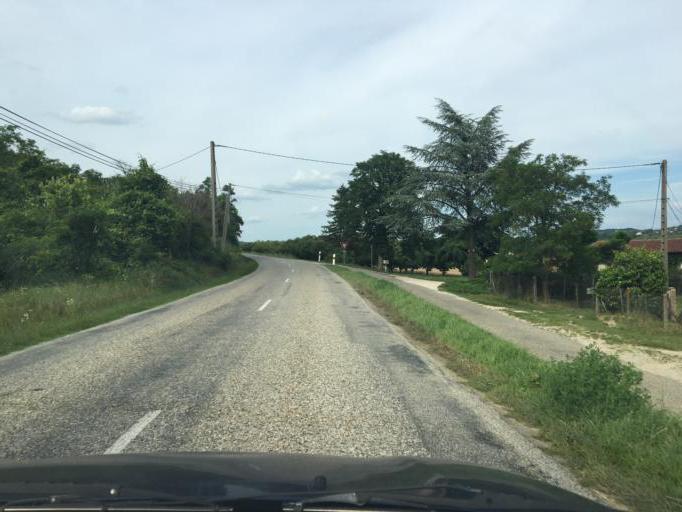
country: FR
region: Rhone-Alpes
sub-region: Departement de la Drome
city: Clerieux
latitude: 45.0989
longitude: 4.9454
